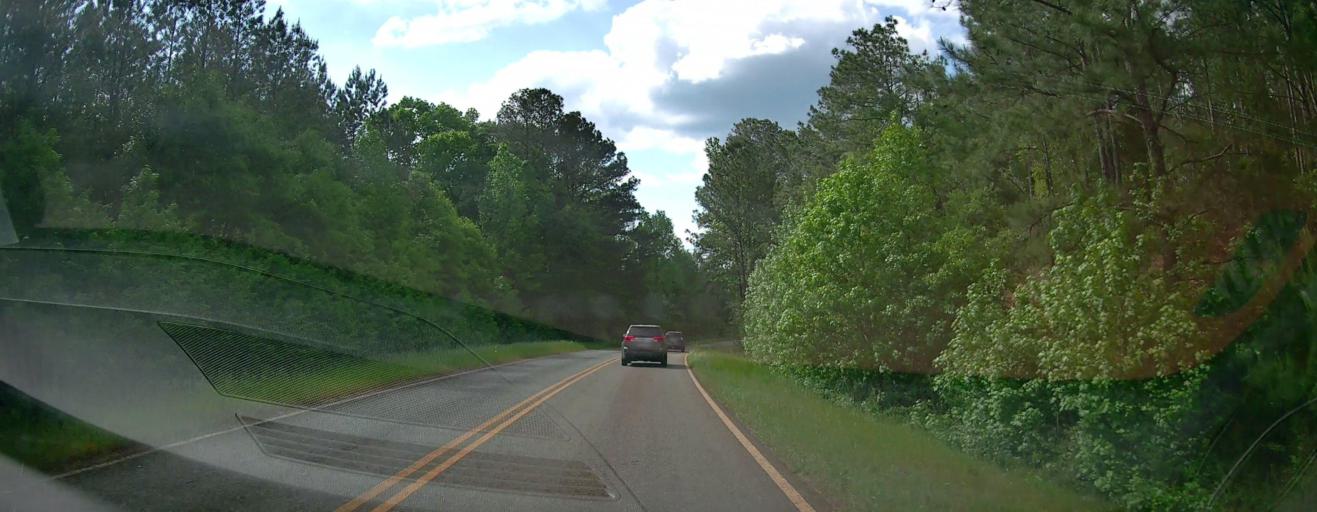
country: US
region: Georgia
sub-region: Laurens County
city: East Dublin
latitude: 32.7394
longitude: -82.9187
